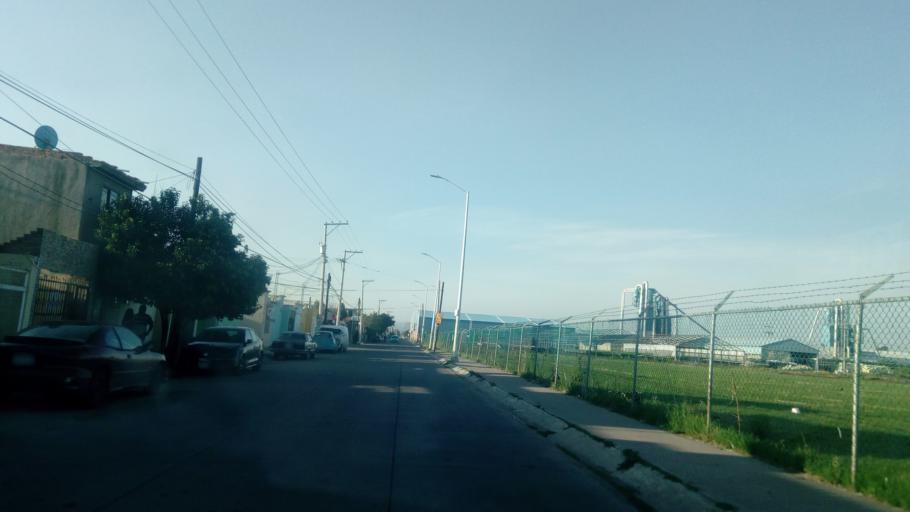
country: MX
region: Durango
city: Victoria de Durango
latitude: 24.0671
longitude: -104.5888
